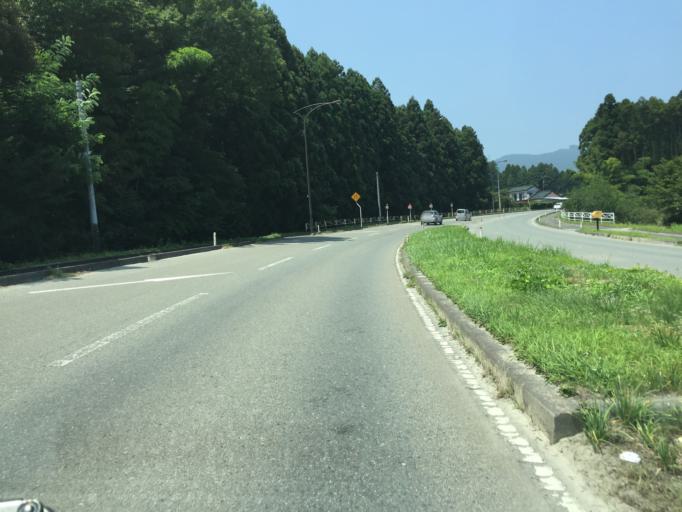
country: JP
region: Miyagi
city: Marumori
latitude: 37.8434
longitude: 140.8911
